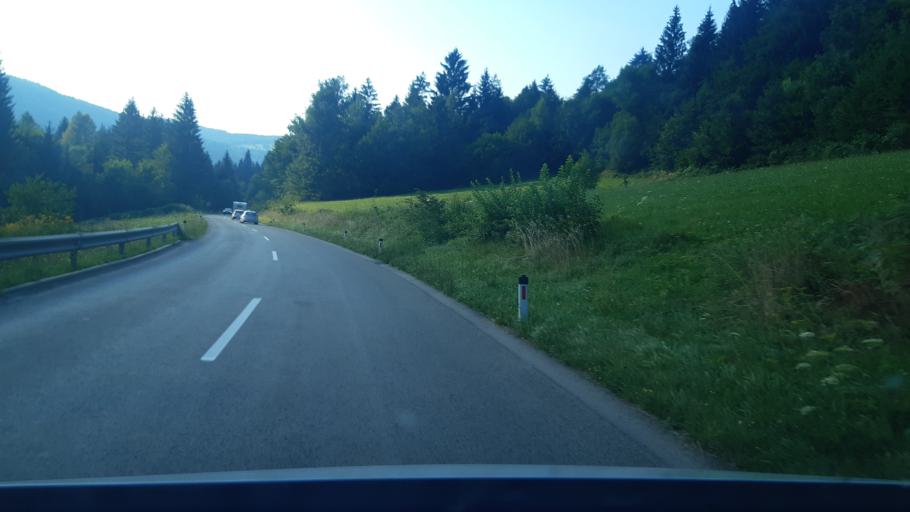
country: SI
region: Semic
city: Semic
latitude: 45.6614
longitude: 15.1139
